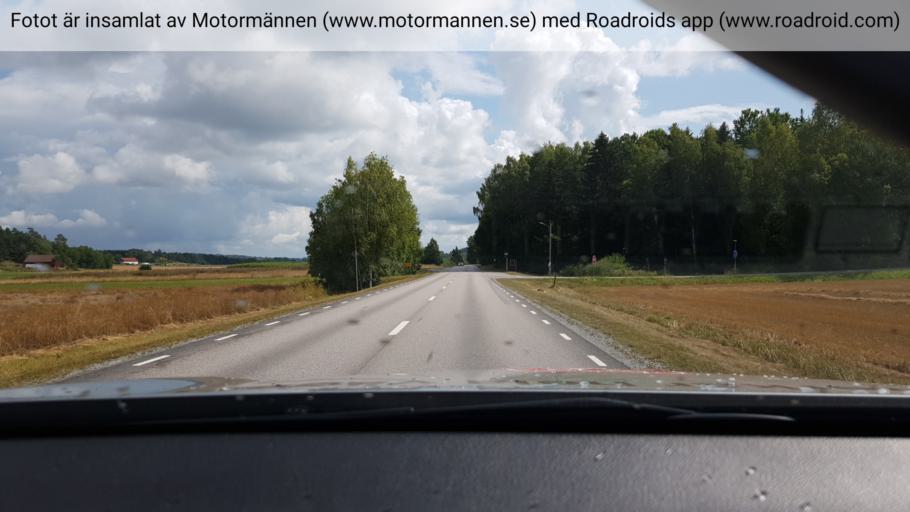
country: SE
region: Stockholm
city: Stenhamra
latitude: 59.3606
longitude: 17.6194
